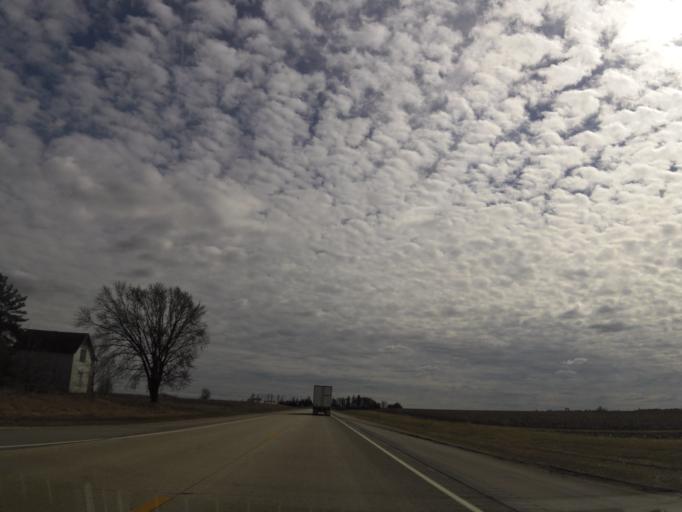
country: US
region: Minnesota
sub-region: Fillmore County
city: Spring Valley
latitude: 43.6728
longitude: -92.3895
